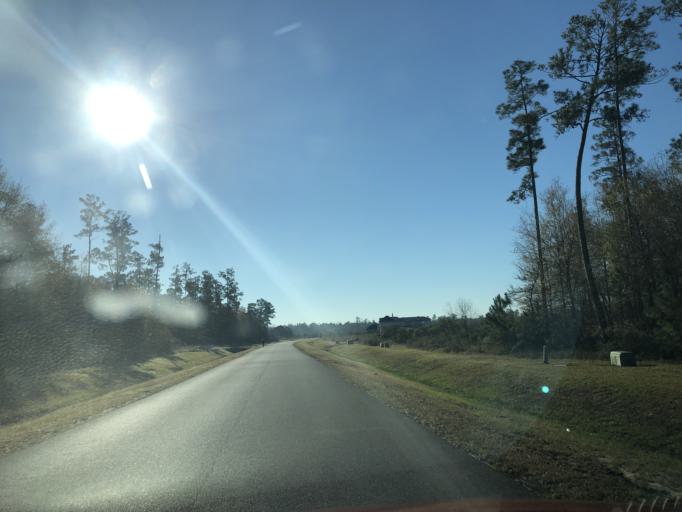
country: US
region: Texas
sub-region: Montgomery County
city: Porter Heights
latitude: 30.0795
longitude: -95.3211
